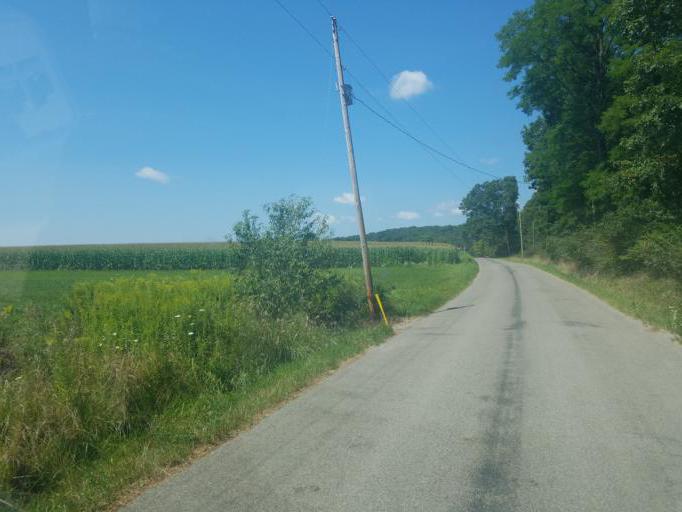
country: US
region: Pennsylvania
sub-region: Clarion County
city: Knox
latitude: 41.1793
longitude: -79.4958
